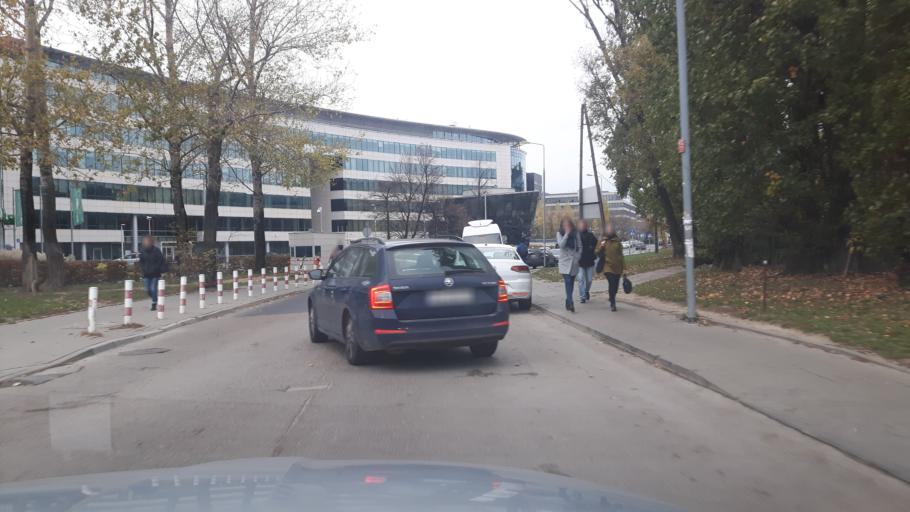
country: PL
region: Masovian Voivodeship
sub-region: Warszawa
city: Ochota
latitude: 52.1821
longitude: 20.9890
